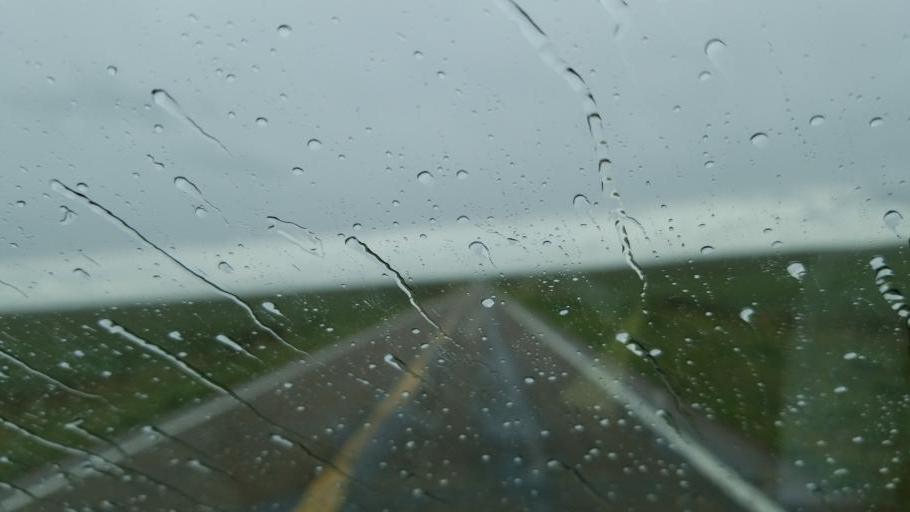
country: US
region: Colorado
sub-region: Lincoln County
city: Hugo
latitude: 38.8498
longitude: -103.2043
